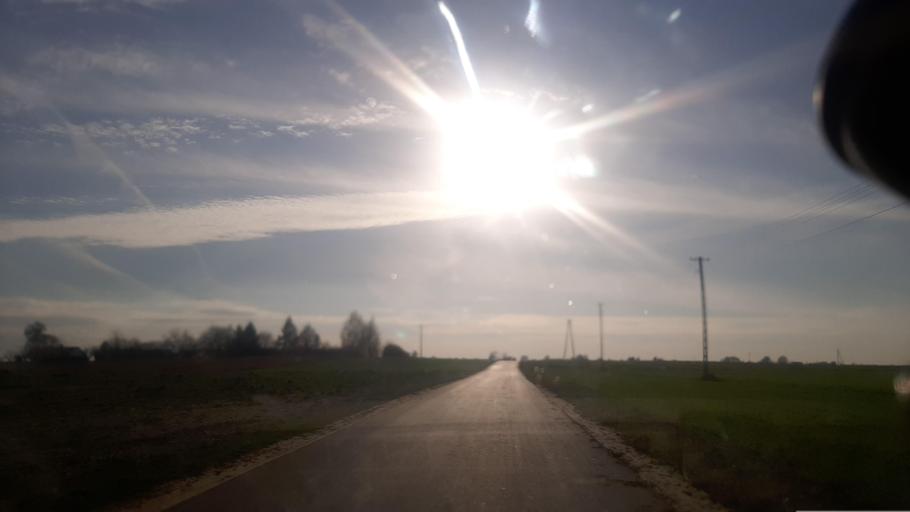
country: PL
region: Lublin Voivodeship
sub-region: Powiat lubelski
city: Garbow
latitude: 51.3940
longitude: 22.3494
